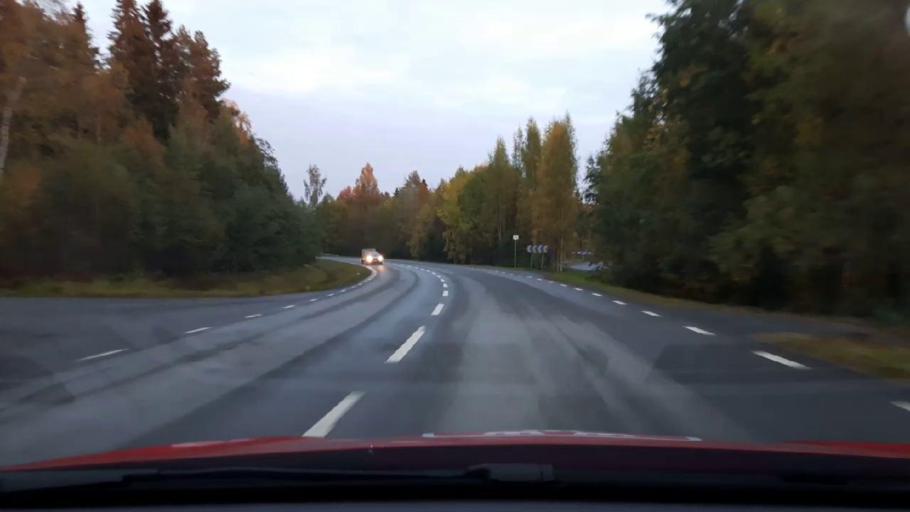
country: SE
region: Jaemtland
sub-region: OEstersunds Kommun
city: Ostersund
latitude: 63.2114
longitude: 14.6268
